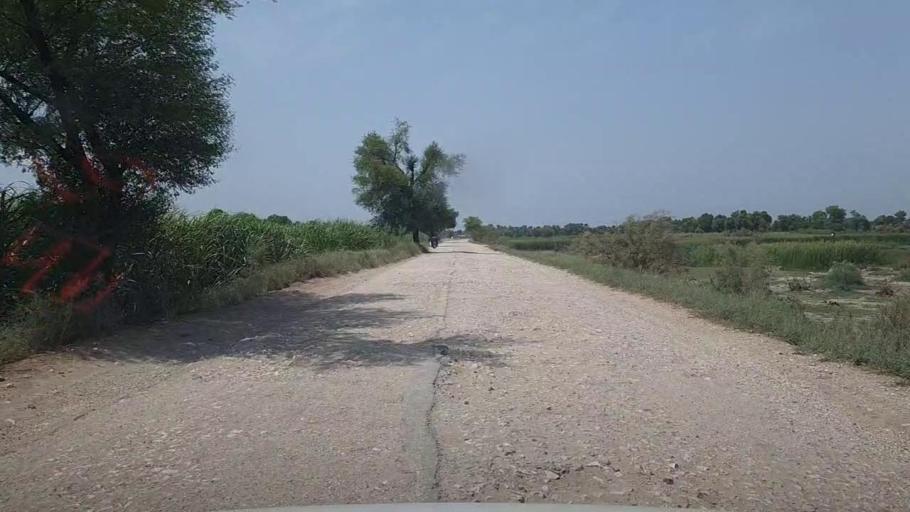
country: PK
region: Sindh
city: Pano Aqil
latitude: 27.8488
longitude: 69.1439
